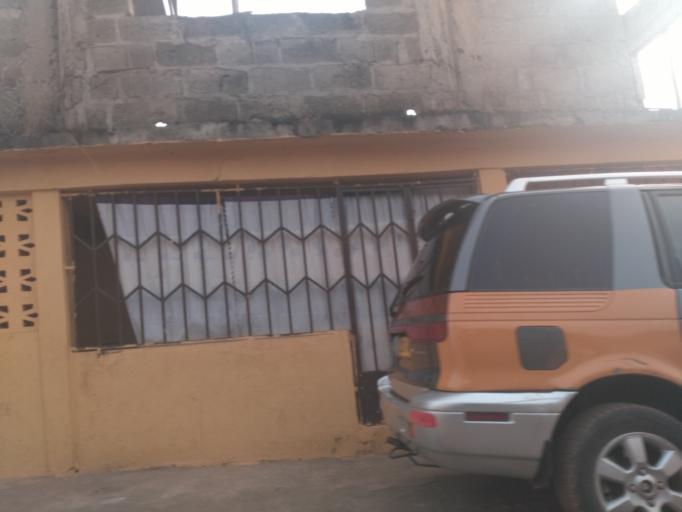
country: GH
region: Ashanti
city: Kumasi
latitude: 6.6988
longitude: -1.6402
